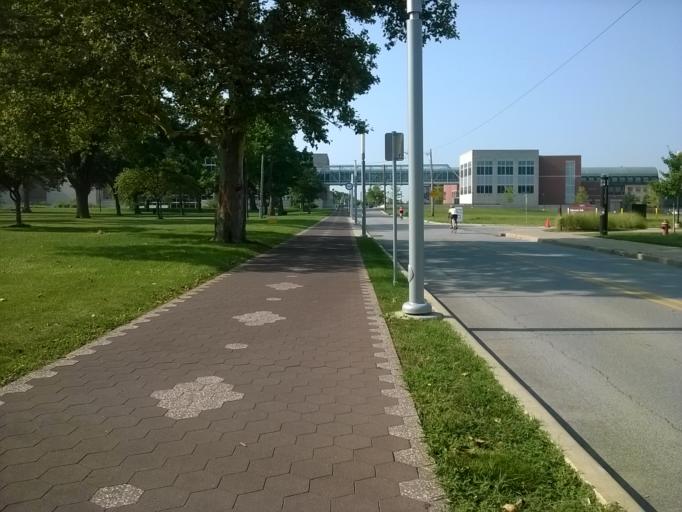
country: US
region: Indiana
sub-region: Marion County
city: Indianapolis
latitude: 39.7709
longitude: -86.1701
